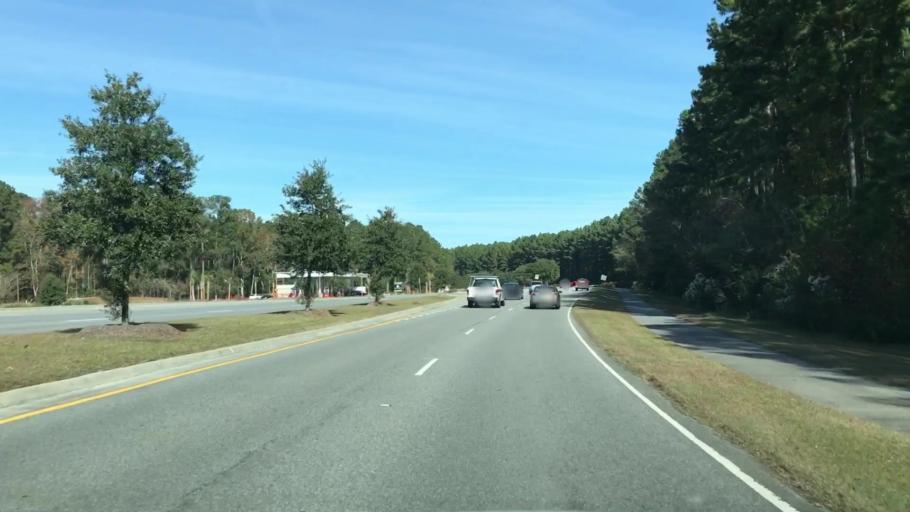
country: US
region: South Carolina
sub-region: Beaufort County
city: Bluffton
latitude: 32.2728
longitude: -80.9148
